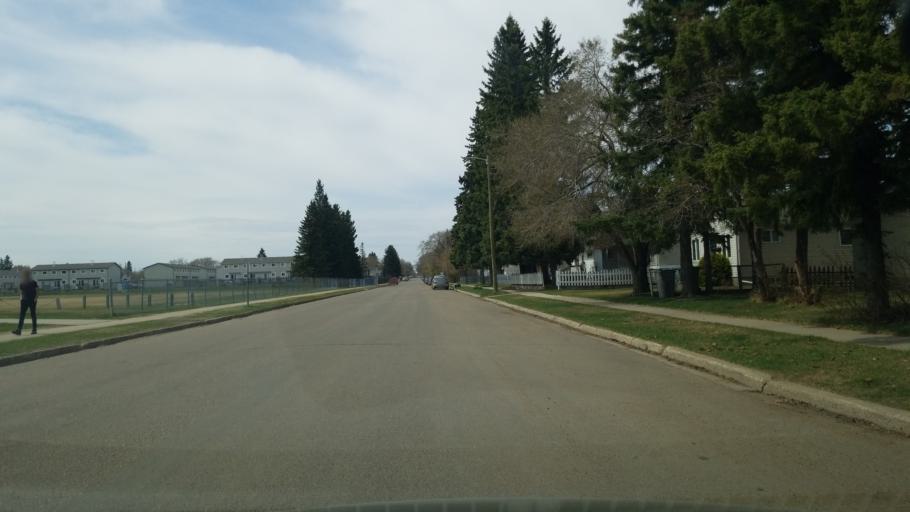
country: CA
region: Saskatchewan
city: Lloydminster
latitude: 53.2825
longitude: -109.9928
